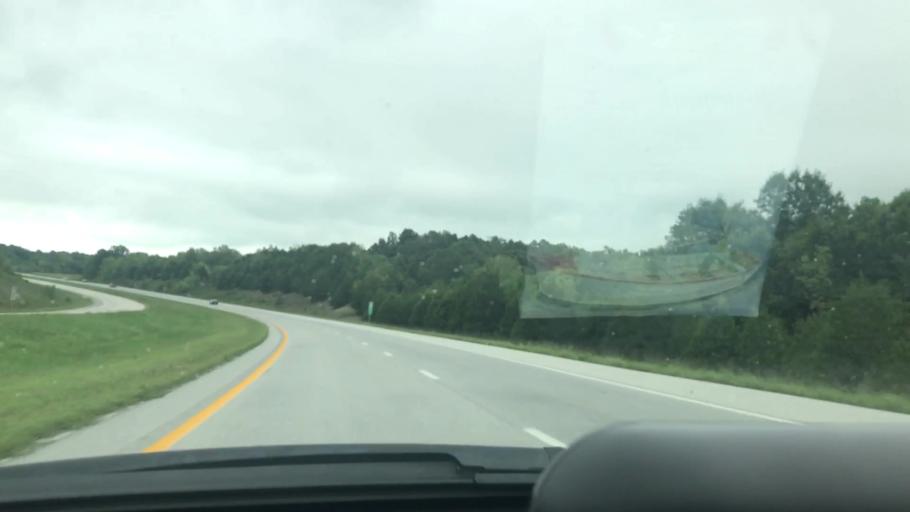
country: US
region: Missouri
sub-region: Greene County
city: Strafford
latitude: 37.2896
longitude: -93.1836
